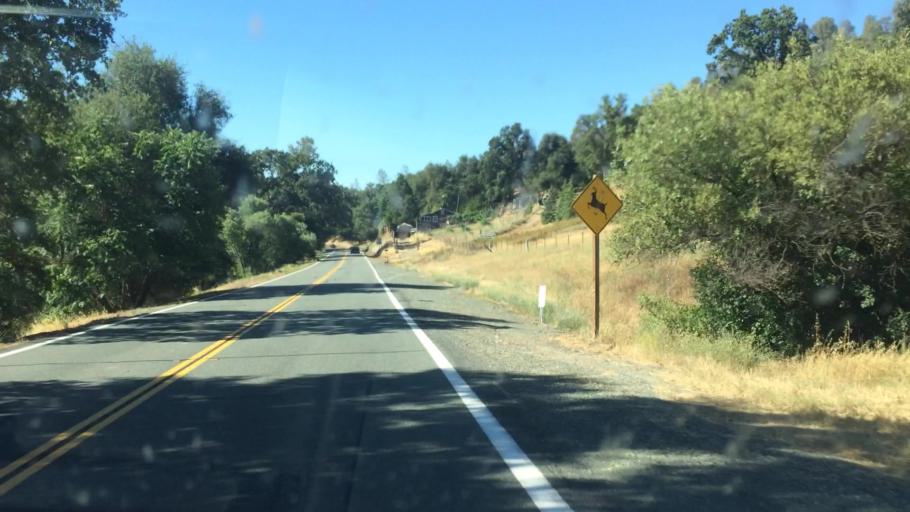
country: US
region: California
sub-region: Amador County
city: Plymouth
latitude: 38.5367
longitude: -120.8476
